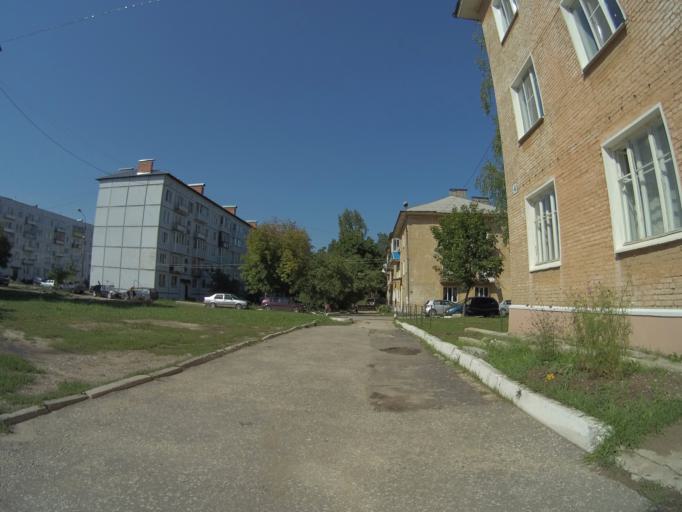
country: RU
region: Vladimir
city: Bogolyubovo
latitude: 56.2528
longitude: 40.5533
